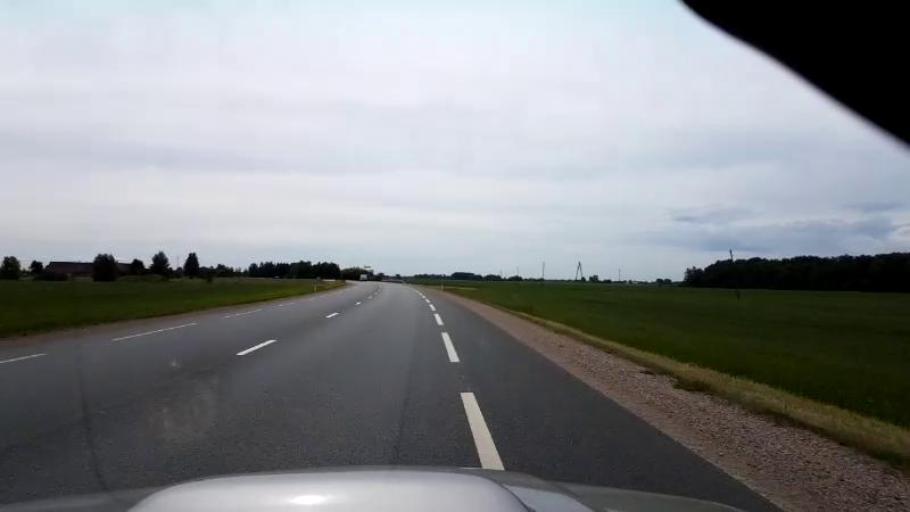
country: LV
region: Bauskas Rajons
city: Bauska
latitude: 56.4442
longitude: 24.1665
